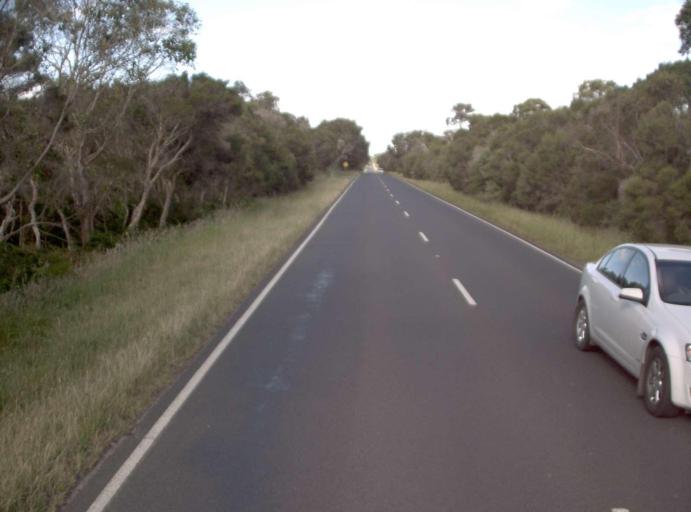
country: AU
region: Victoria
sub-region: Bass Coast
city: North Wonthaggi
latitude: -38.5979
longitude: 145.7826
